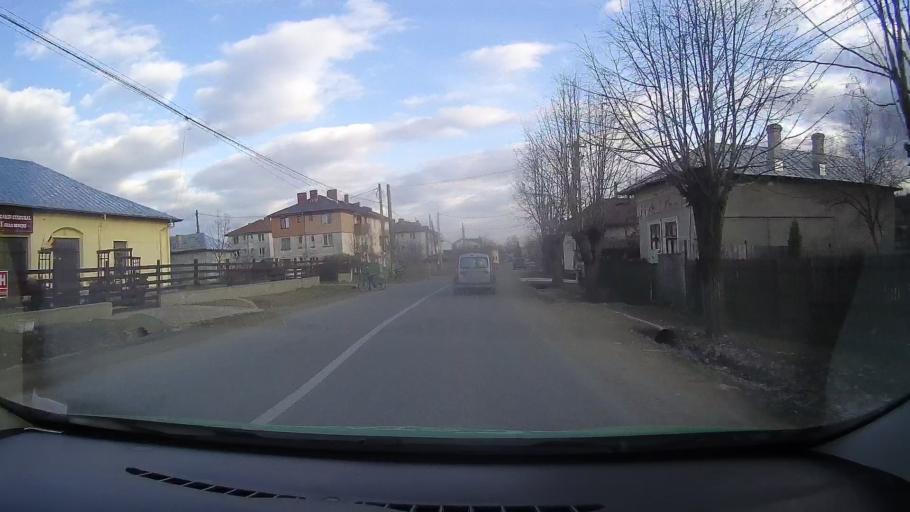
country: RO
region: Dambovita
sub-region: Comuna Gura Ocnitei
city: Gura Ocnitei
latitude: 44.9454
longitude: 25.5607
